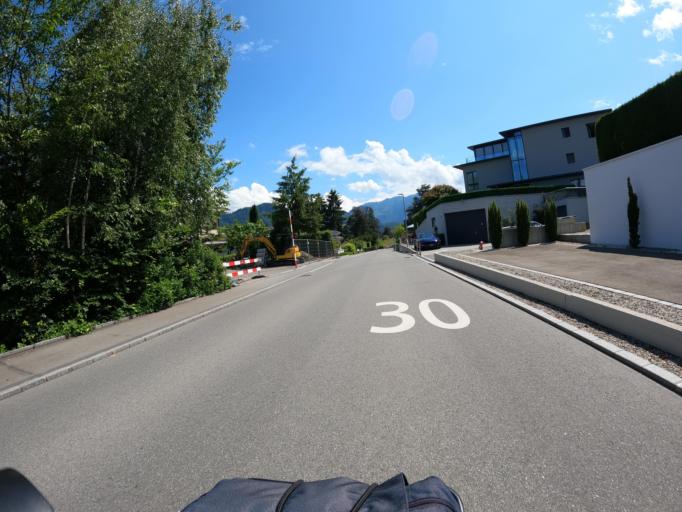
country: CH
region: Lucerne
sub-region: Lucerne-Land District
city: Horw
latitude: 47.0128
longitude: 8.3382
